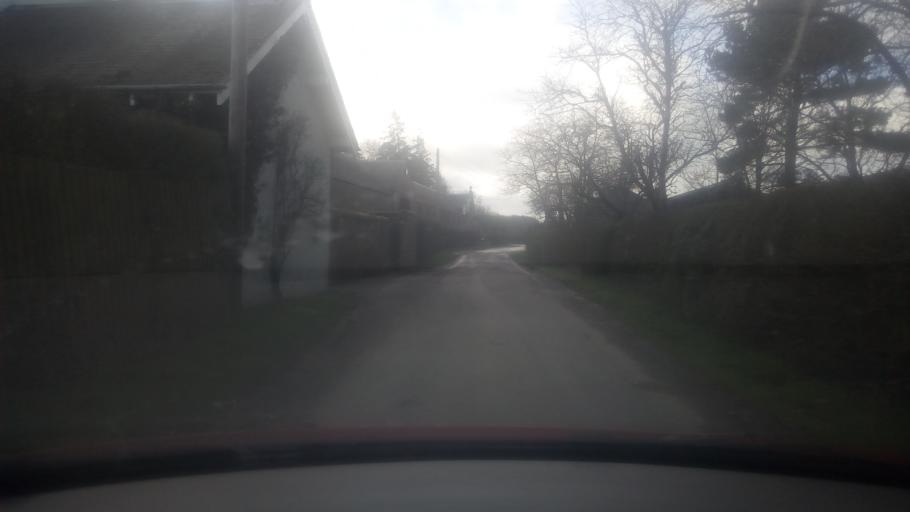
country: GB
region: Scotland
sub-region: The Scottish Borders
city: Saint Boswells
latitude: 55.5209
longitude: -2.6522
